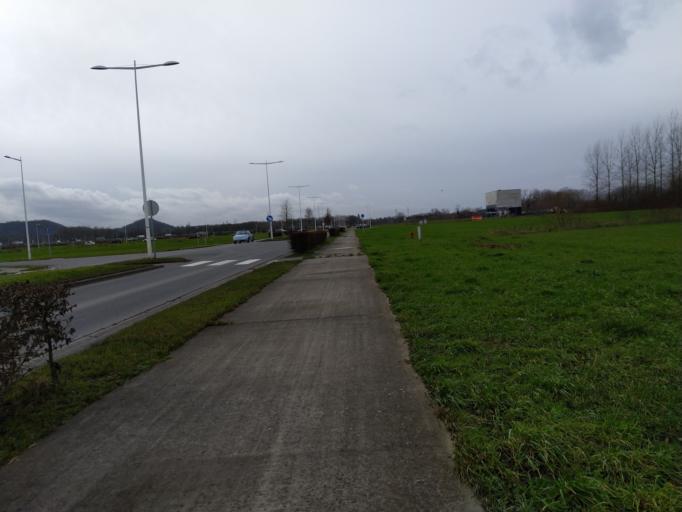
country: BE
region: Wallonia
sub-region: Province du Hainaut
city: Mons
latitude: 50.4619
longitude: 3.9191
